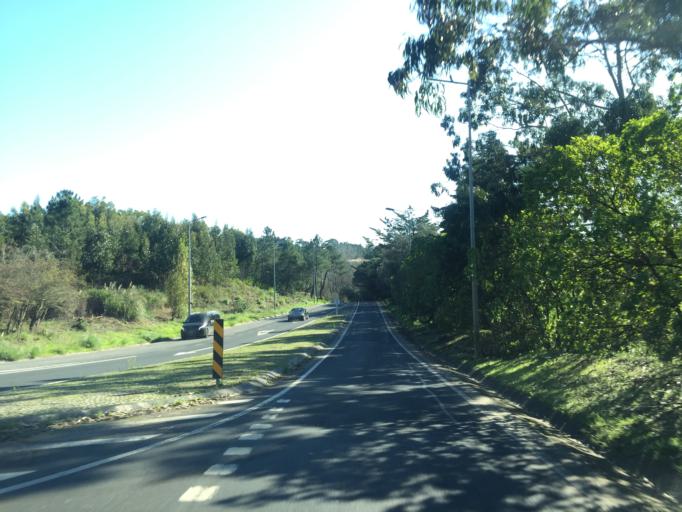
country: PT
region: Lisbon
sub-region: Sintra
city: Belas
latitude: 38.8013
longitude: -9.2817
